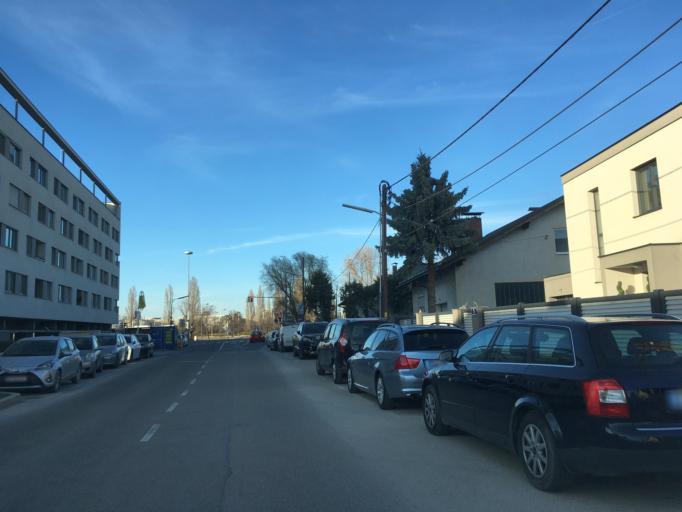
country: AT
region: Lower Austria
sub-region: Politischer Bezirk Ganserndorf
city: Gross-Enzersdorf
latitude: 48.2148
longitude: 16.5041
